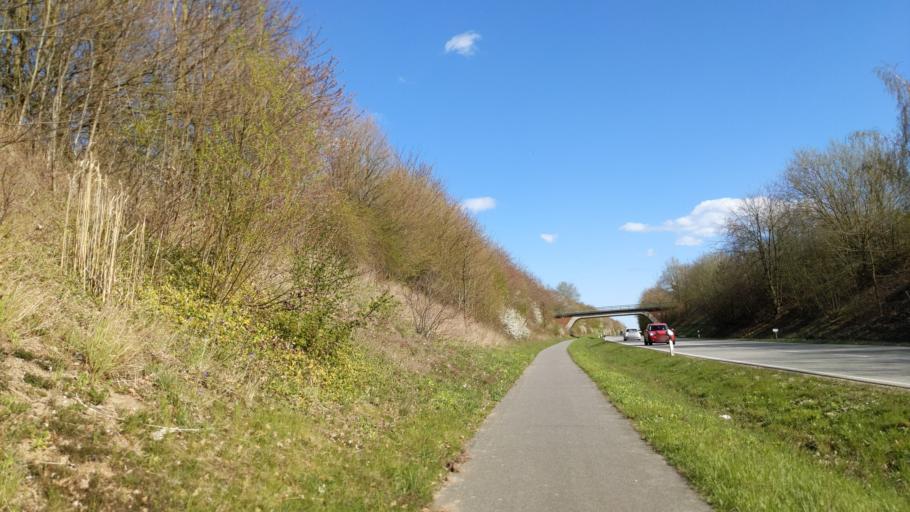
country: DE
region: Schleswig-Holstein
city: Eutin
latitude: 54.1224
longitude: 10.6017
